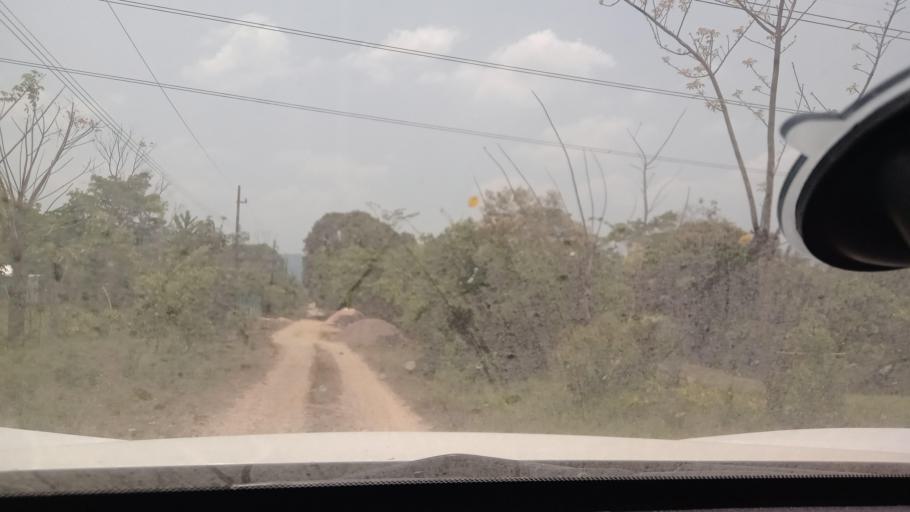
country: MX
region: Chiapas
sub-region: Tecpatan
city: Raudales Malpaso
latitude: 17.4422
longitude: -93.7882
